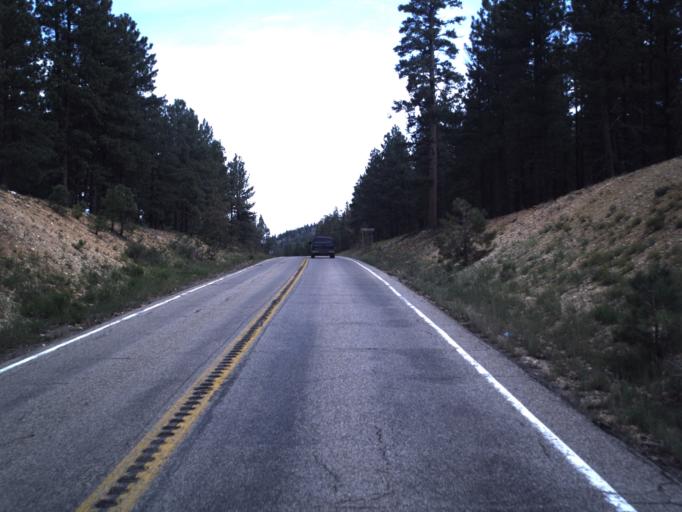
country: US
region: Utah
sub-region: Garfield County
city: Panguitch
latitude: 37.4960
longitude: -112.6207
